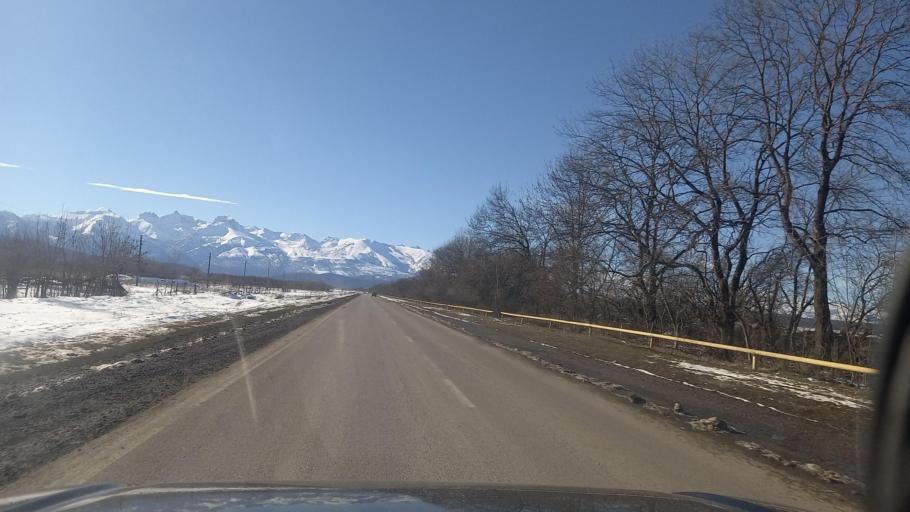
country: RU
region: North Ossetia
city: Chikola
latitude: 43.1839
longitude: 43.8955
